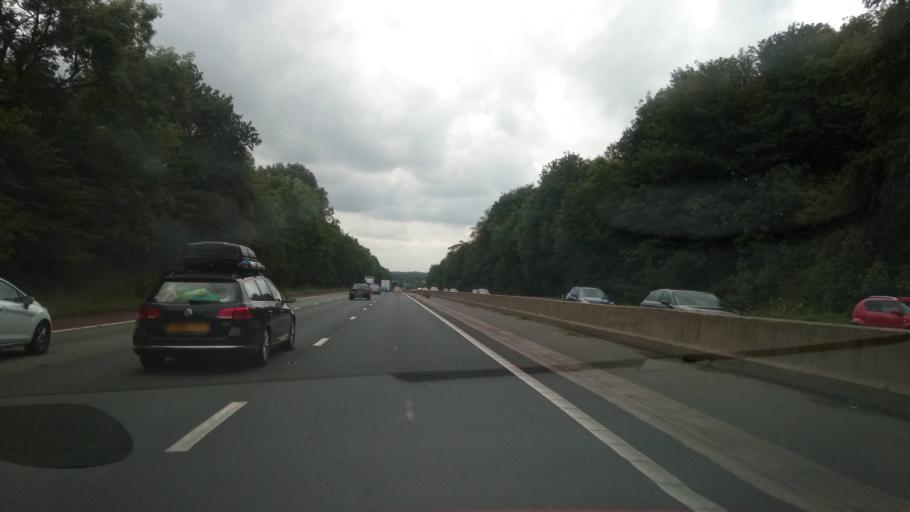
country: GB
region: England
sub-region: Lancashire
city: Galgate
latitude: 54.0140
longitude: -2.7818
